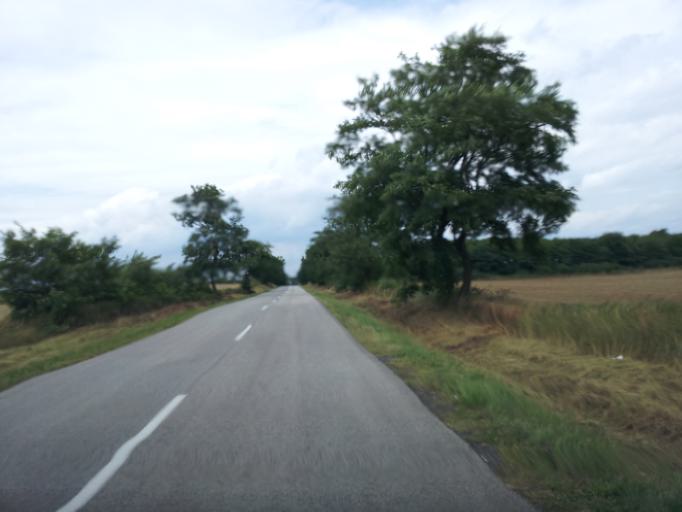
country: HU
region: Zala
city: Zalaszentgrot
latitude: 47.0246
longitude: 16.9745
